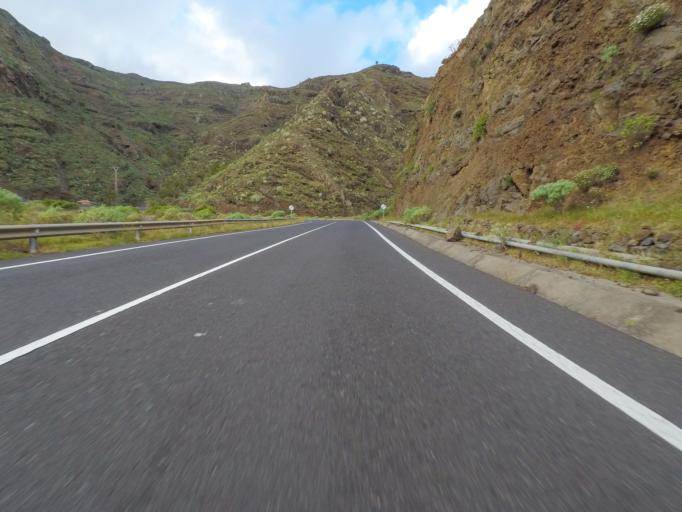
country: ES
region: Canary Islands
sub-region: Provincia de Santa Cruz de Tenerife
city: San Sebastian de la Gomera
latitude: 28.1241
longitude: -17.1468
